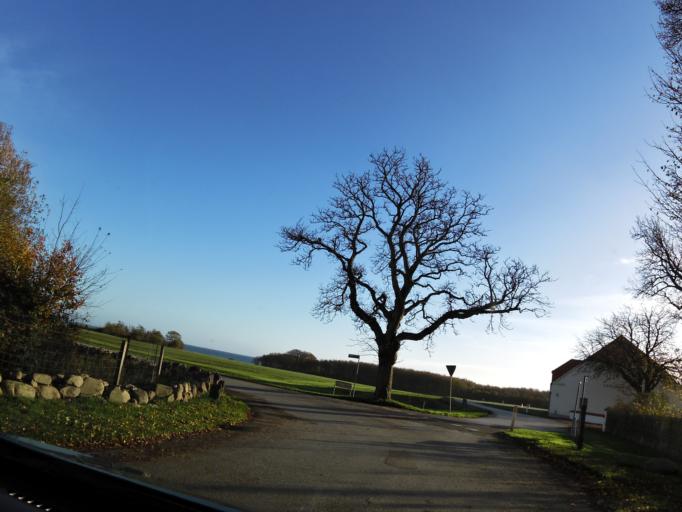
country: DK
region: Central Jutland
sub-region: Odder Kommune
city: Odder
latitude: 55.9147
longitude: 10.2341
